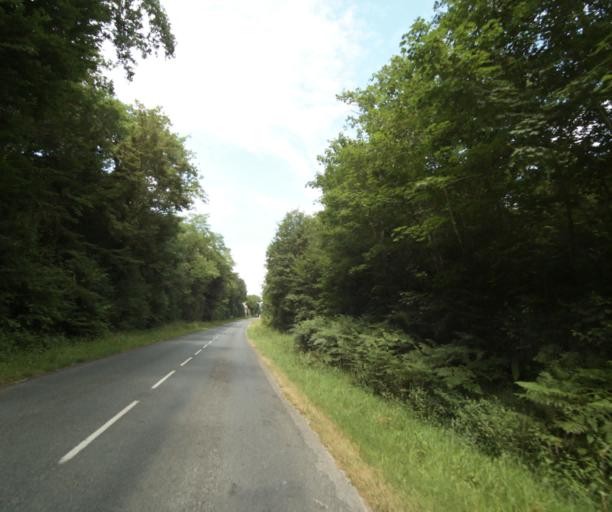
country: FR
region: Ile-de-France
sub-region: Departement de Seine-et-Marne
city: Chailly-en-Biere
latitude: 48.4861
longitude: 2.6283
